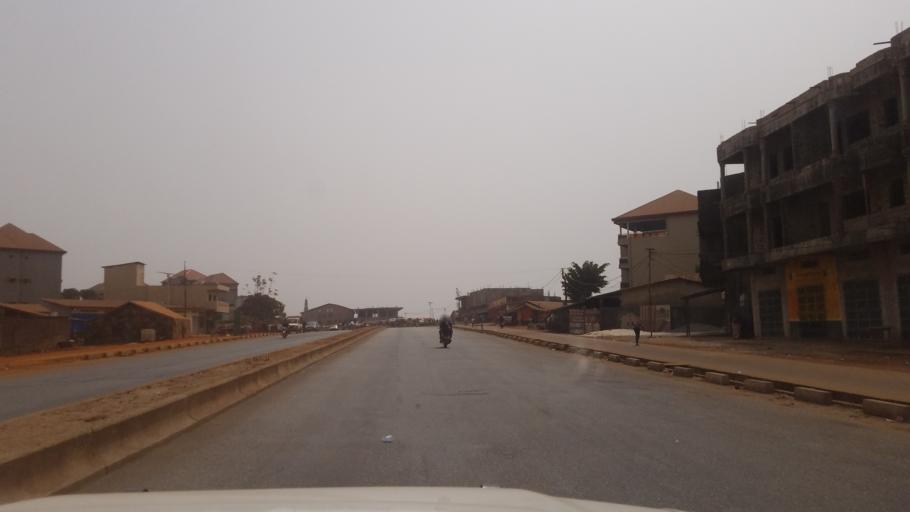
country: GN
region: Kindia
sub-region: Prefecture de Dubreka
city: Dubreka
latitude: 9.6820
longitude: -13.5273
